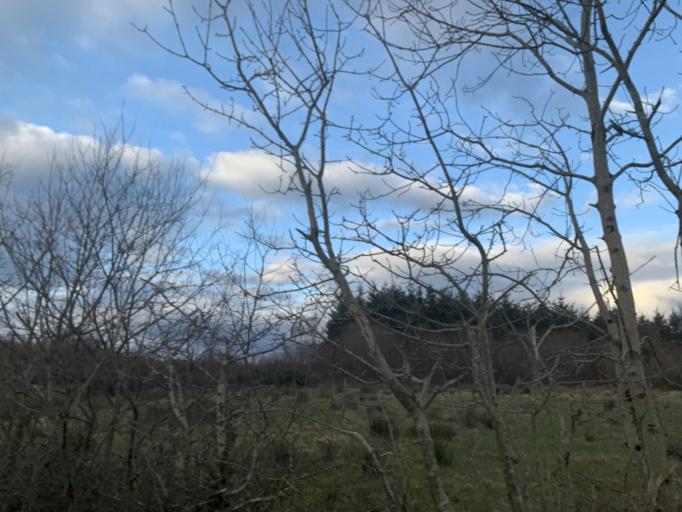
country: IE
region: Connaught
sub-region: Maigh Eo
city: Ballyhaunis
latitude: 53.8628
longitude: -8.7513
